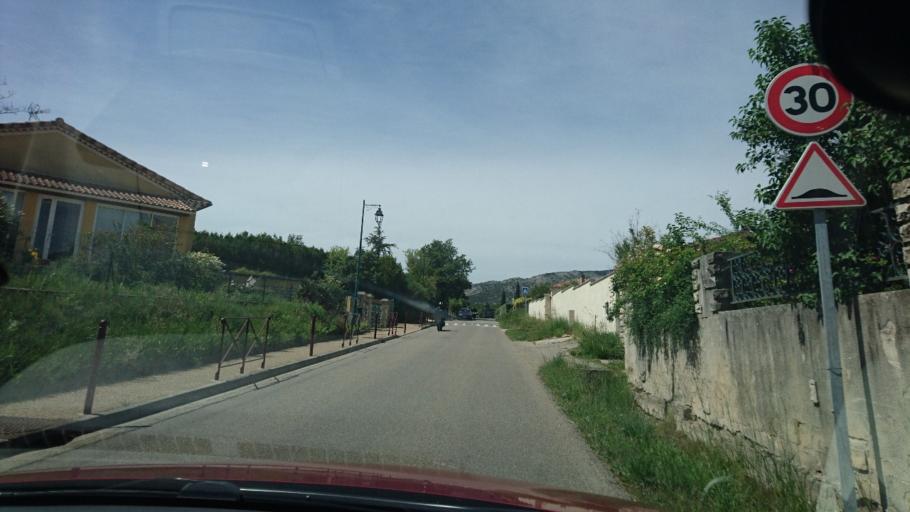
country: FR
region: Provence-Alpes-Cote d'Azur
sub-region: Departement du Vaucluse
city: Bedoin
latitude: 44.1267
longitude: 5.1790
